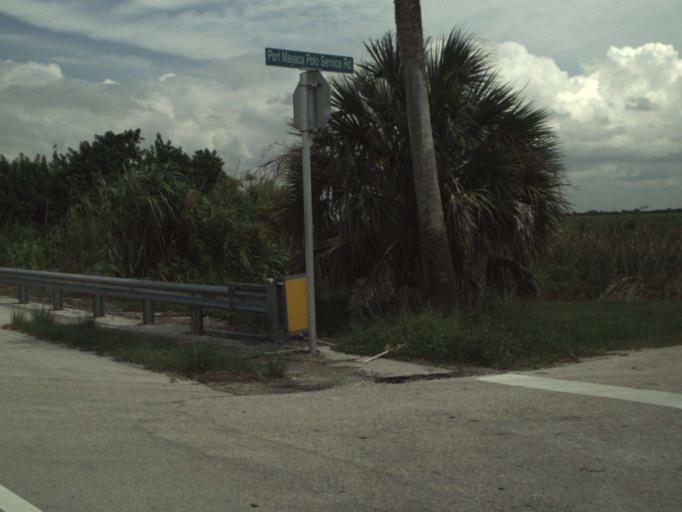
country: US
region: Florida
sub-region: Martin County
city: Indiantown
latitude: 27.0593
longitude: -80.6473
